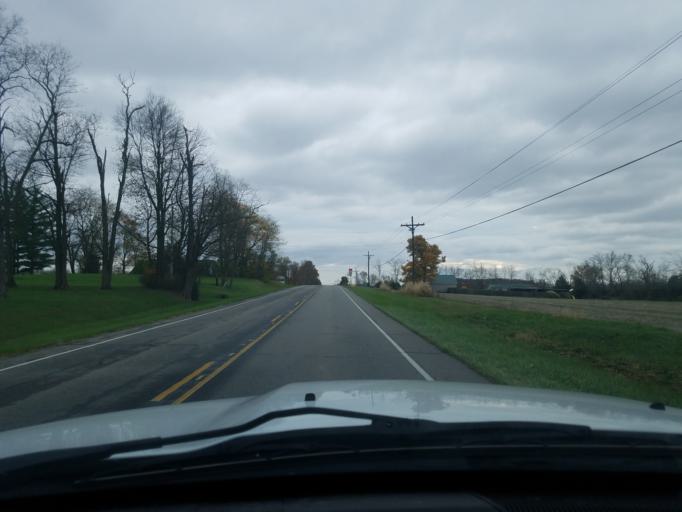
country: US
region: Indiana
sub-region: Bartholomew County
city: Hope
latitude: 39.2560
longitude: -85.7716
